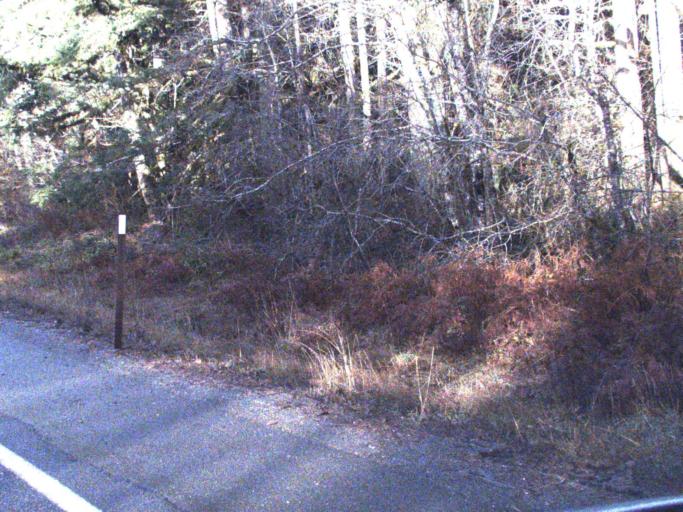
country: US
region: Washington
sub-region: Snohomish County
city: Darrington
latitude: 48.2640
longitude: -121.6366
